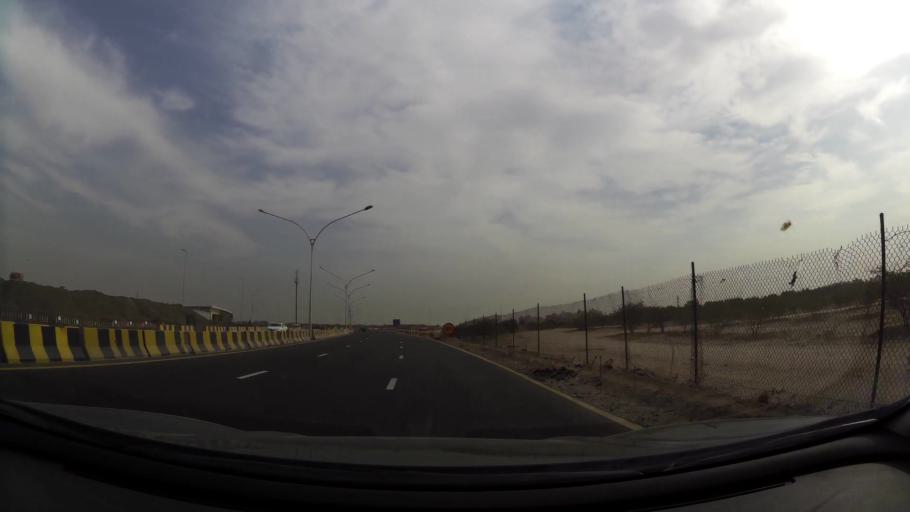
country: KW
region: Muhafazat al Jahra'
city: Al Jahra'
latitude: 29.3336
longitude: 47.7961
